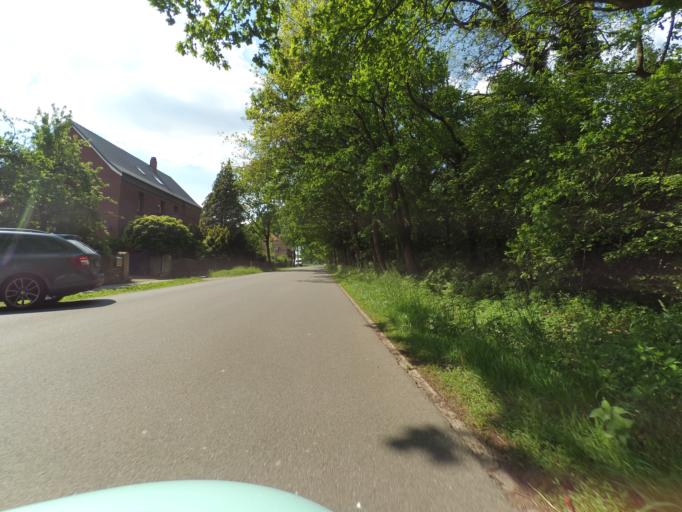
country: DE
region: Lower Saxony
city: Haenigsen
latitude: 52.4641
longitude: 10.1274
